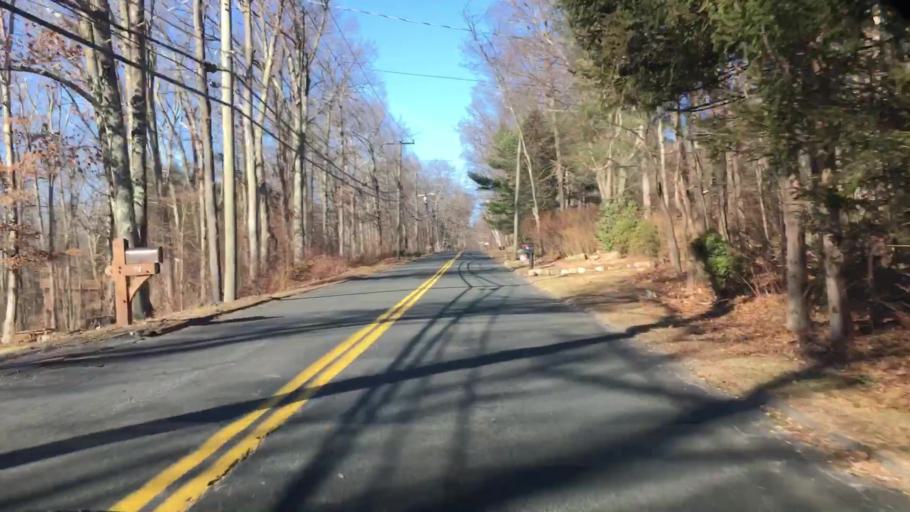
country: US
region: Connecticut
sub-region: Tolland County
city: Crystal Lake
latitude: 41.9353
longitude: -72.3876
